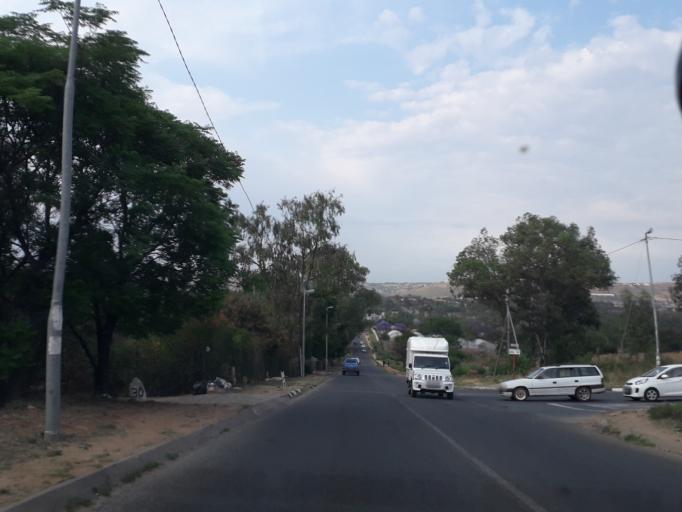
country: ZA
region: Gauteng
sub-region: West Rand District Municipality
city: Muldersdriseloop
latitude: -26.0765
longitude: 27.9102
